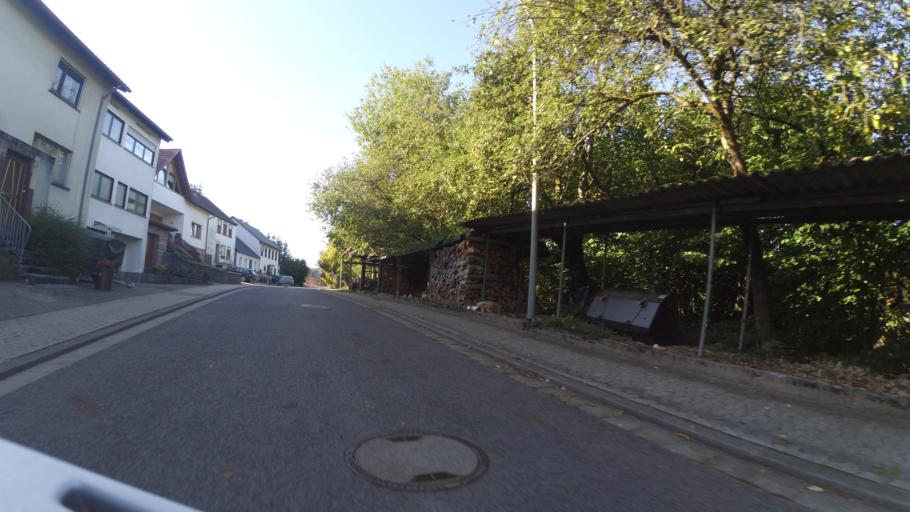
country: DE
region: Saarland
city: Eppelborn
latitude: 49.4350
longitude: 6.9484
